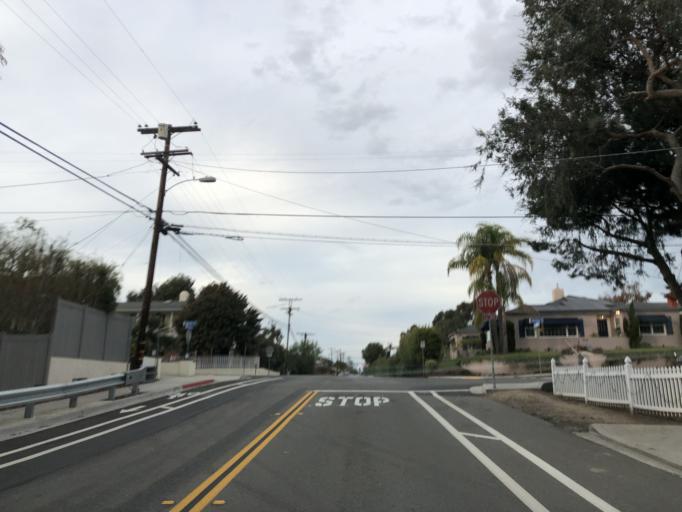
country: US
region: California
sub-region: San Diego County
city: San Diego
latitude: 32.7429
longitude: -117.1512
